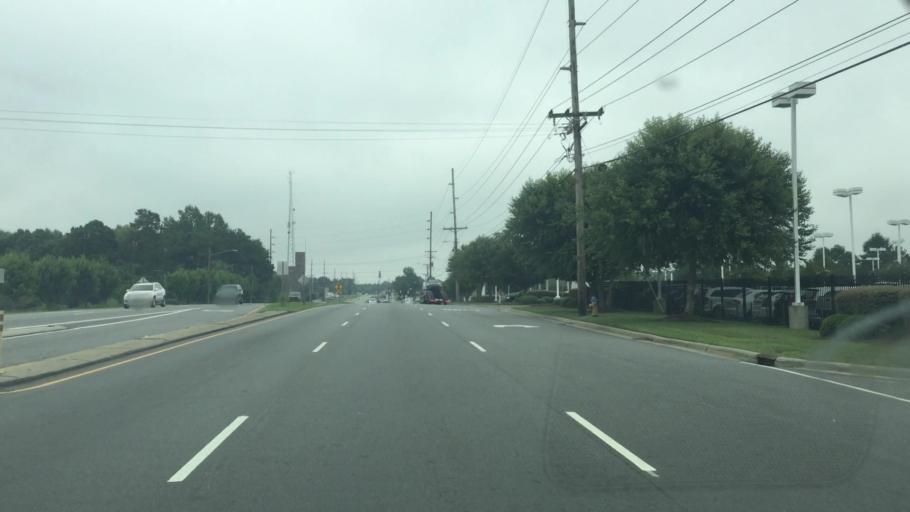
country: US
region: North Carolina
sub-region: Cabarrus County
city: Concord
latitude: 35.4033
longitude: -80.6095
